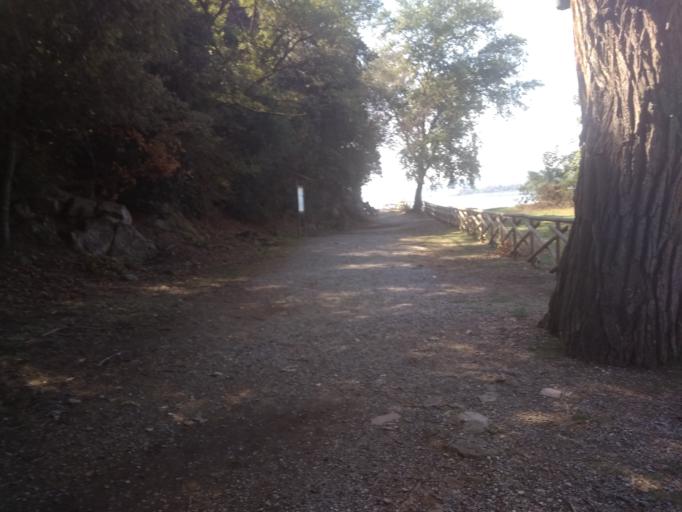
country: IT
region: Umbria
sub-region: Provincia di Perugia
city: Tuoro sul Trasimeno
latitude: 43.1785
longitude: 12.0920
